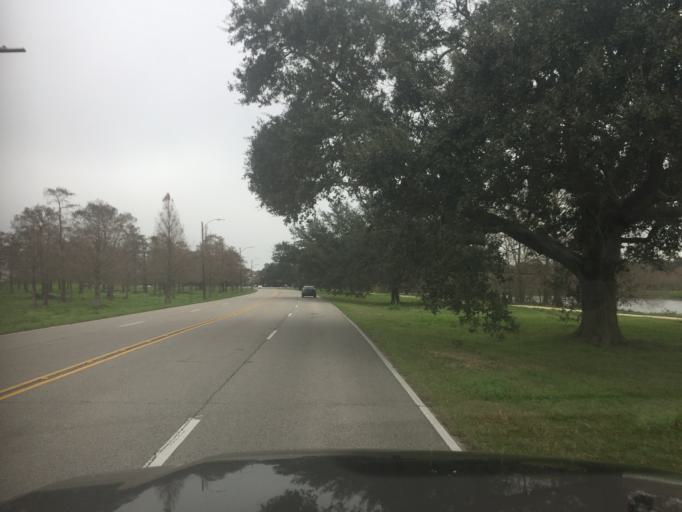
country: US
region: Louisiana
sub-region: Jefferson Parish
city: Metairie
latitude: 30.0159
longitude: -90.0971
